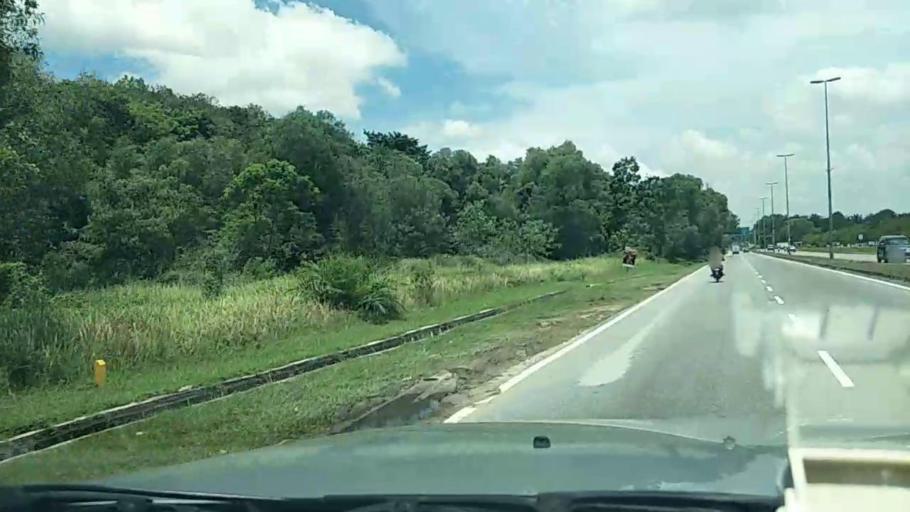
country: MY
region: Selangor
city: Subang Jaya
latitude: 2.9726
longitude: 101.6125
